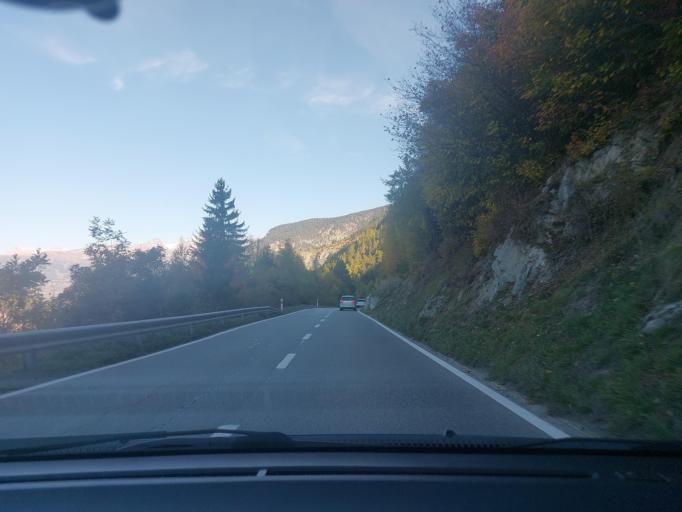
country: CH
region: Valais
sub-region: Sierre District
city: Chippis
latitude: 46.2368
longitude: 7.5784
